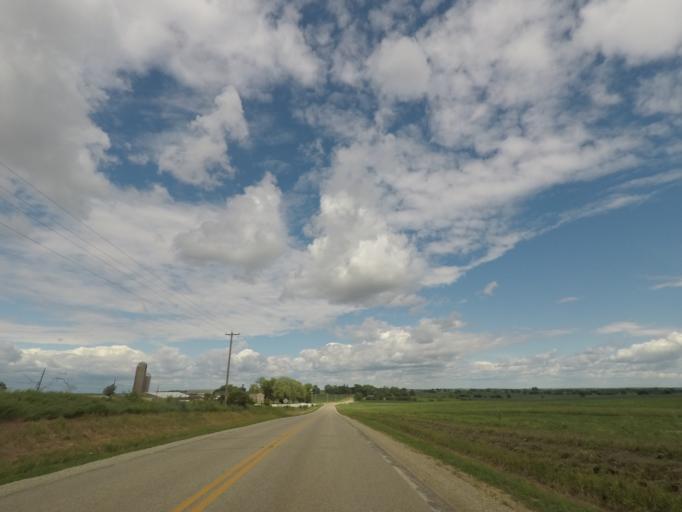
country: US
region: Wisconsin
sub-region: Rock County
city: Orfordville
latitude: 42.7147
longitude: -89.2340
